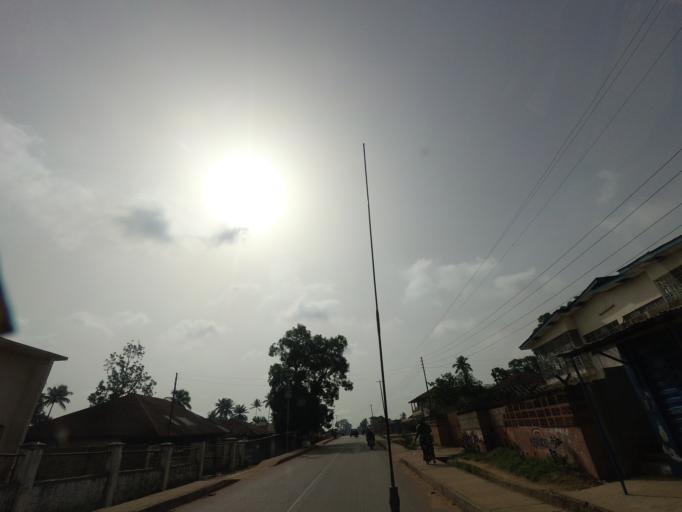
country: SL
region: Southern Province
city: Bo
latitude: 7.9584
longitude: -11.7477
